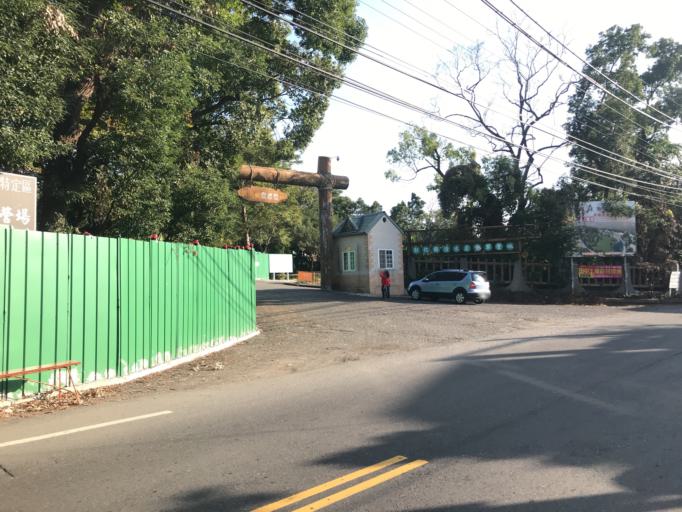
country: TW
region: Taiwan
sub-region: Nantou
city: Nantou
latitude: 23.8853
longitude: 120.6081
